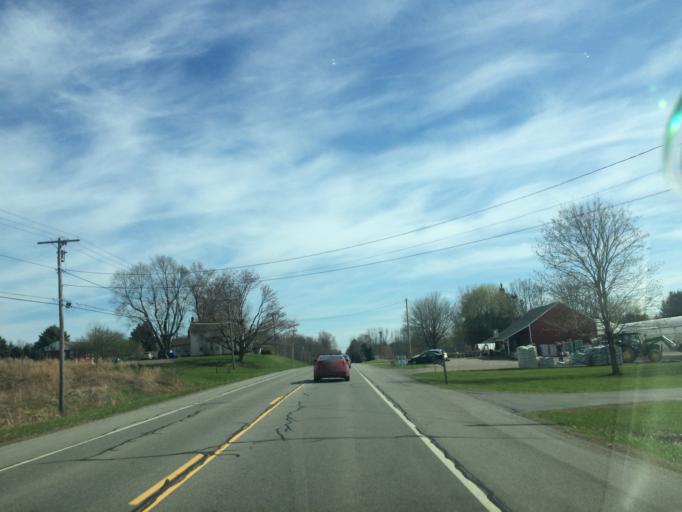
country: US
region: New York
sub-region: Monroe County
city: Webster
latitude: 43.1896
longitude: -77.4305
